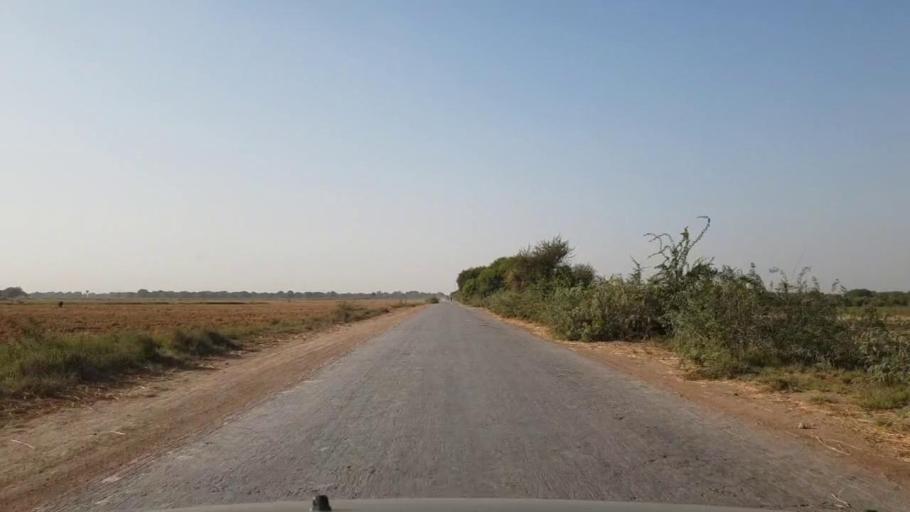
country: PK
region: Sindh
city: Chambar
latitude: 25.2005
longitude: 68.7952
